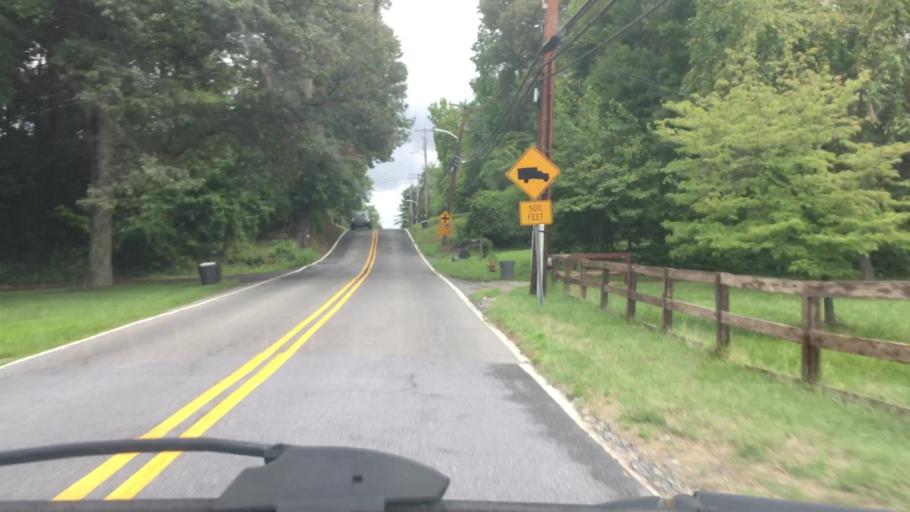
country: US
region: Maryland
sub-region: Prince George's County
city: Glenn Dale
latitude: 39.0015
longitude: -76.7783
